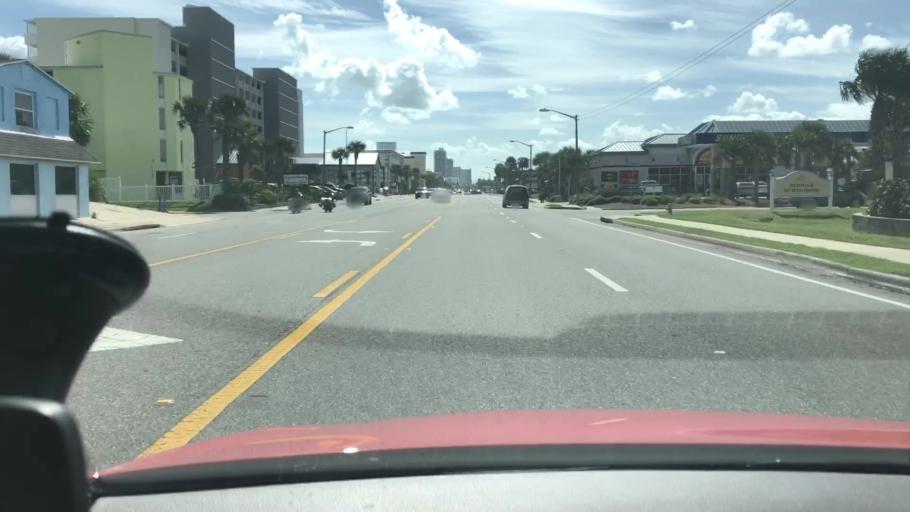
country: US
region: Florida
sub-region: Volusia County
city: Ormond Beach
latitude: 29.2808
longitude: -81.0345
